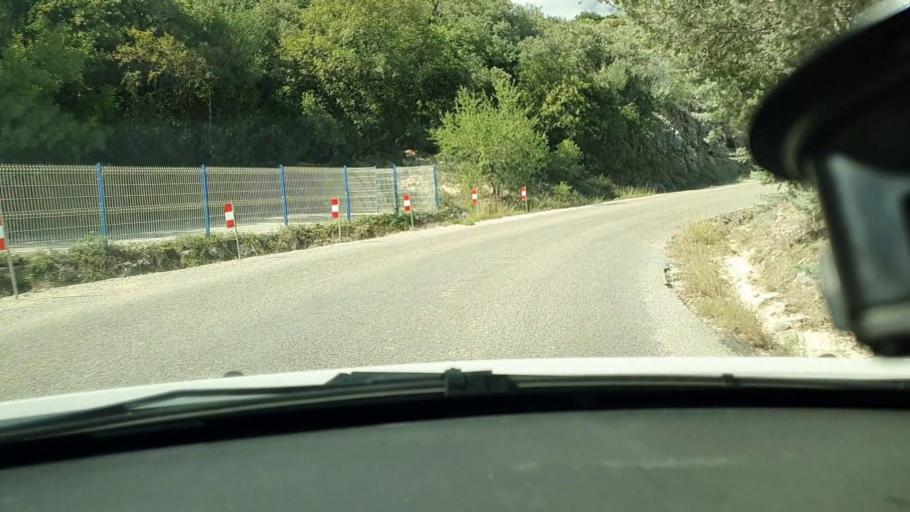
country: FR
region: Languedoc-Roussillon
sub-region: Departement du Gard
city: Goudargues
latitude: 44.1647
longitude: 4.4370
